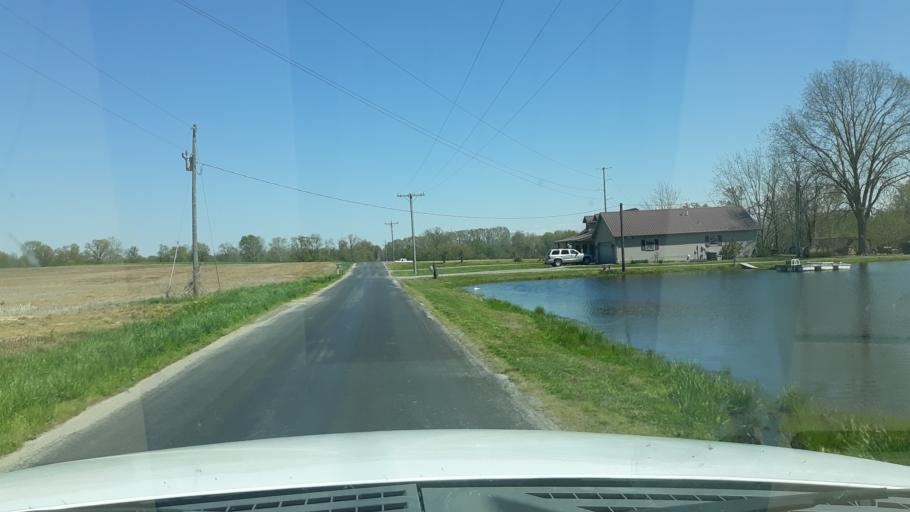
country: US
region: Illinois
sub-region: Saline County
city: Harrisburg
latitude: 37.8341
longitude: -88.6253
